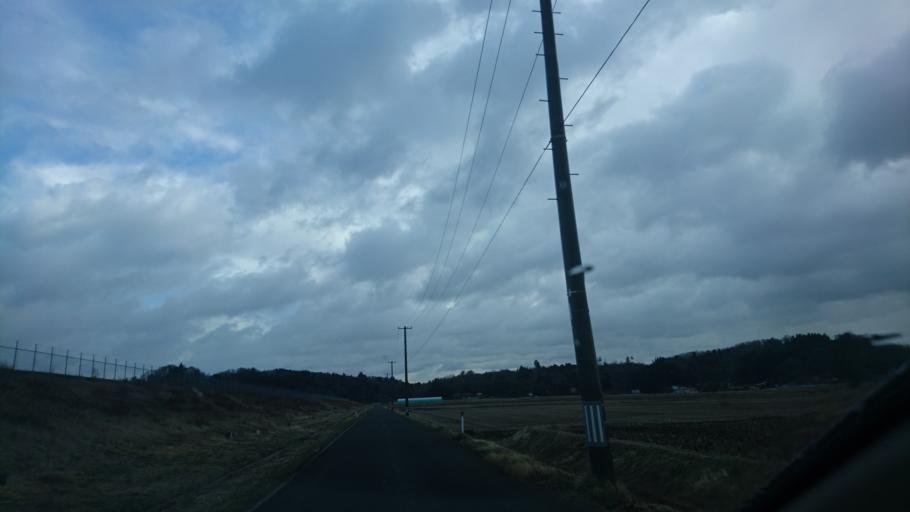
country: JP
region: Iwate
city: Ichinoseki
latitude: 38.7806
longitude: 141.0328
